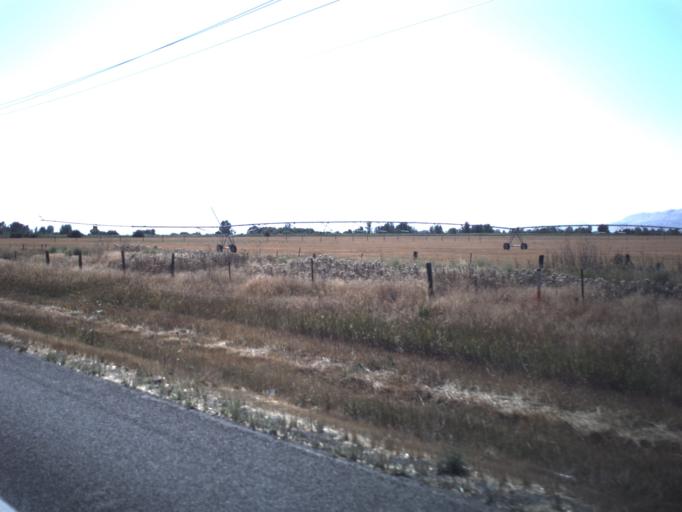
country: US
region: Utah
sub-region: Cache County
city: Richmond
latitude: 41.9662
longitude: -111.8130
